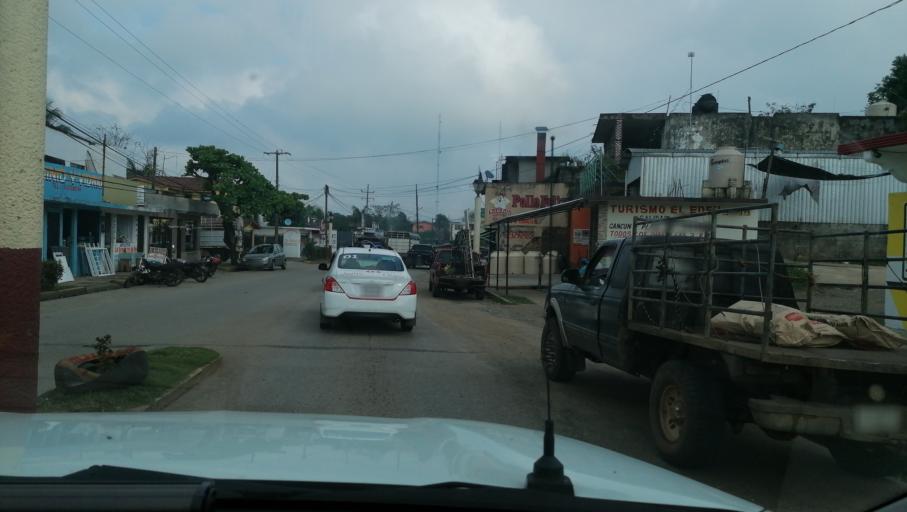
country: MX
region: Chiapas
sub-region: Juarez
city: El Triunfo 1ra. Seccion (Cardona)
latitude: 17.6068
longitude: -93.1918
